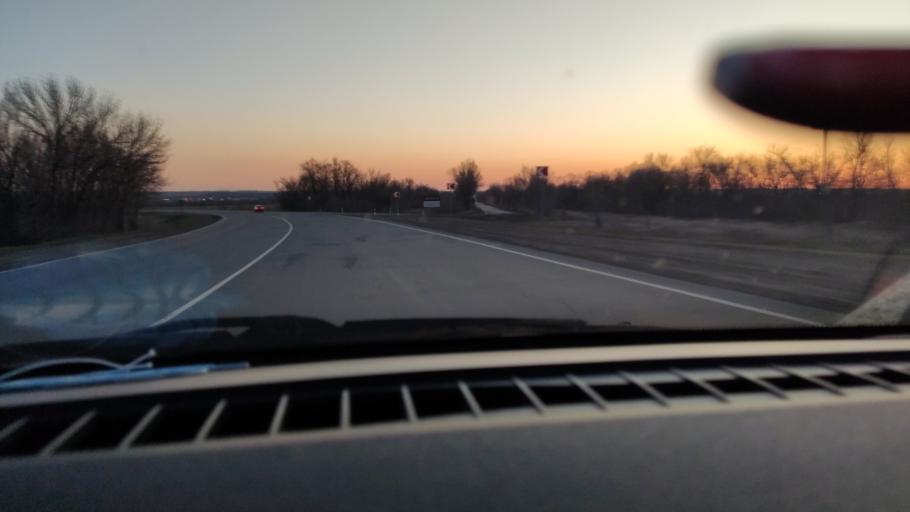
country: RU
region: Saratov
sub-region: Saratovskiy Rayon
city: Saratov
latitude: 51.7153
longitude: 46.0251
